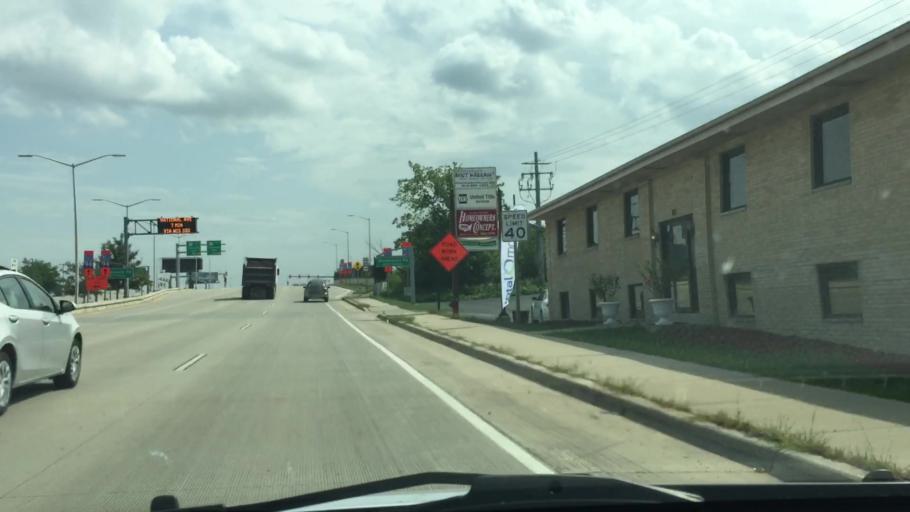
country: US
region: Wisconsin
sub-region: Waukesha County
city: Elm Grove
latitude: 43.0379
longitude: -88.0473
